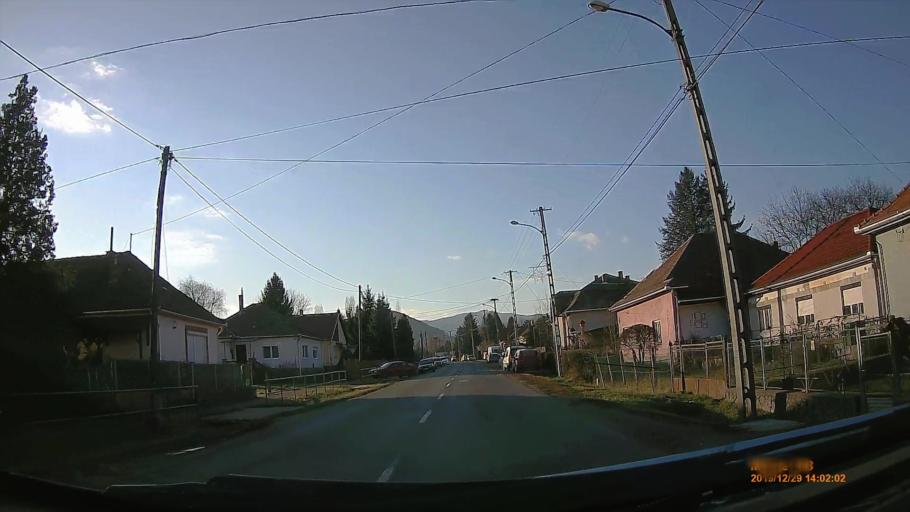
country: HU
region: Heves
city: Parad
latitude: 47.9239
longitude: 20.0438
